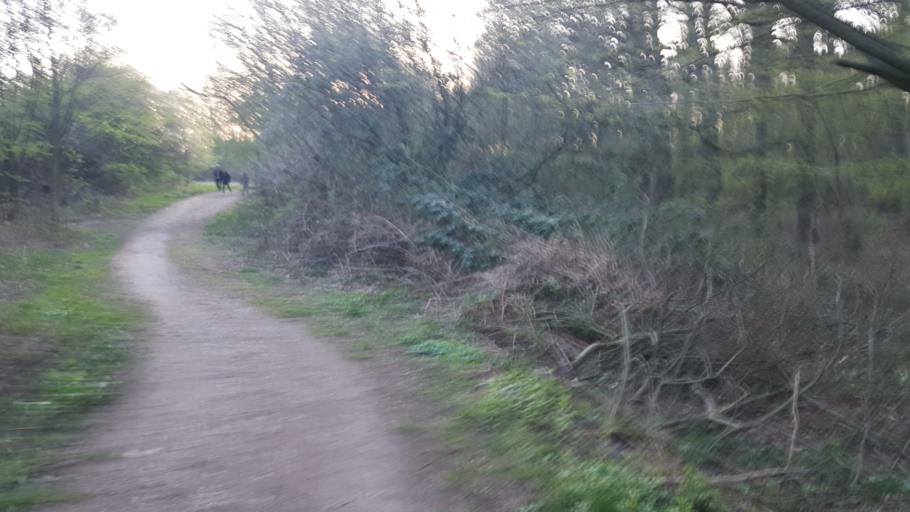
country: DE
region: Lower Saxony
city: Isernhagen Farster Bauerschaft
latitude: 52.4417
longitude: 9.8505
